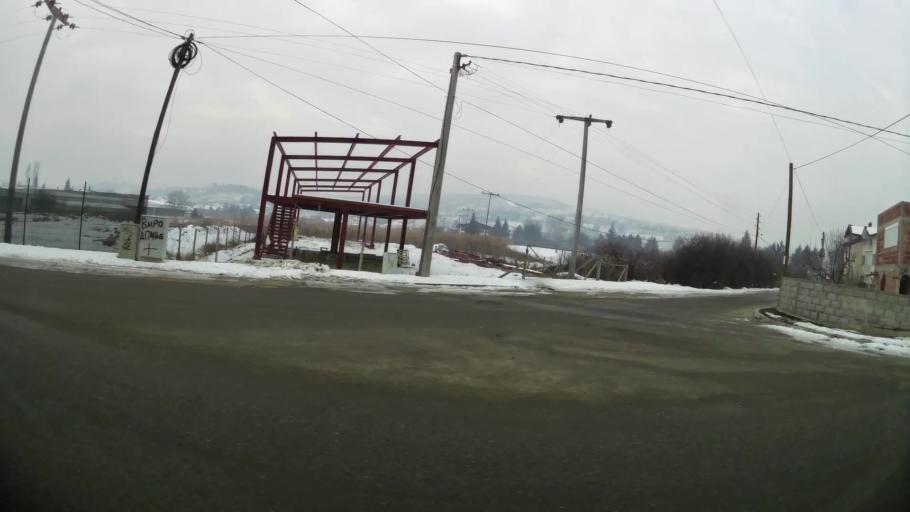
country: MK
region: Saraj
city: Saraj
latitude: 42.0311
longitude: 21.3446
